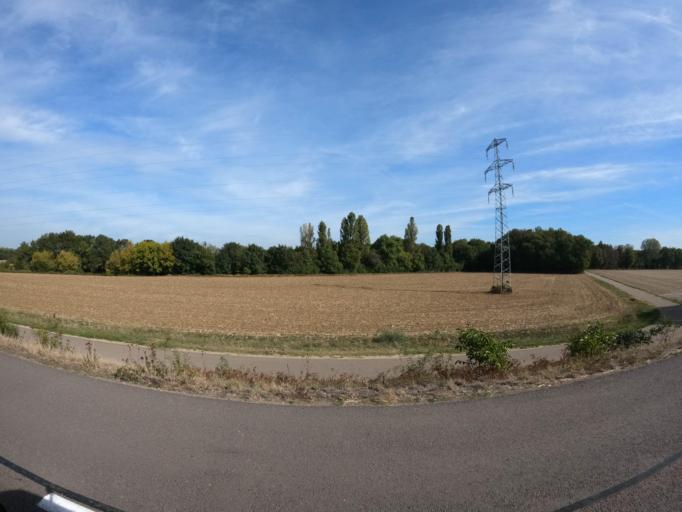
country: FR
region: Bourgogne
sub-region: Departement de Saone-et-Loire
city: Saint-Remy
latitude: 46.7587
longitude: 4.8498
